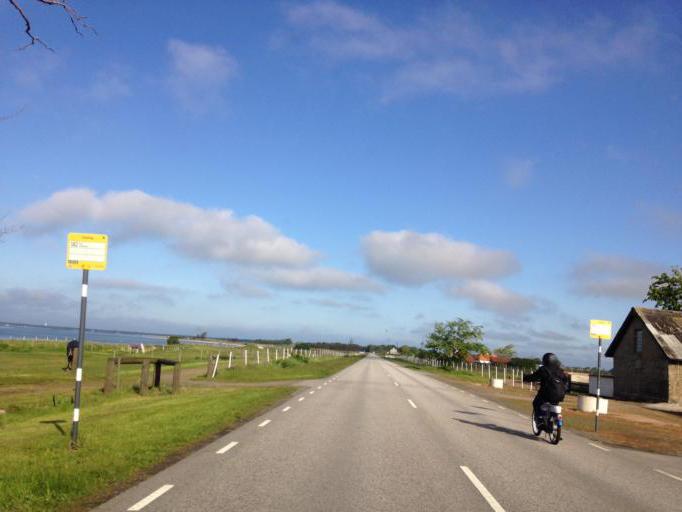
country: SE
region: Skane
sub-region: Trelleborgs Kommun
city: Skare
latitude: 55.3880
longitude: 13.0146
